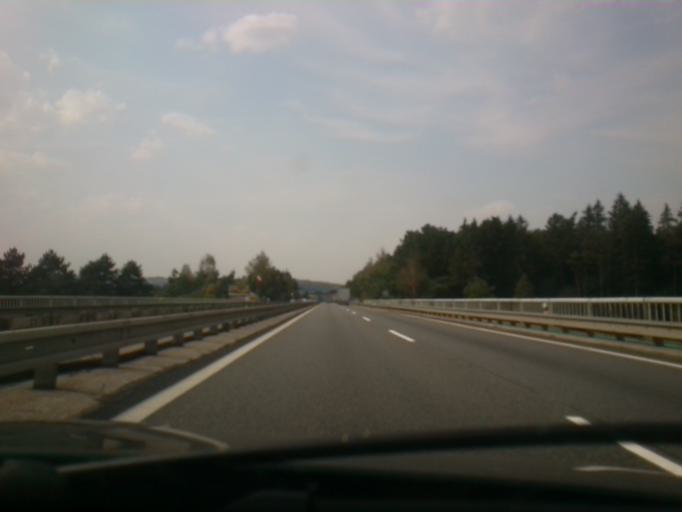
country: CZ
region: Central Bohemia
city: Ondrejov
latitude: 49.8997
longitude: 14.7405
